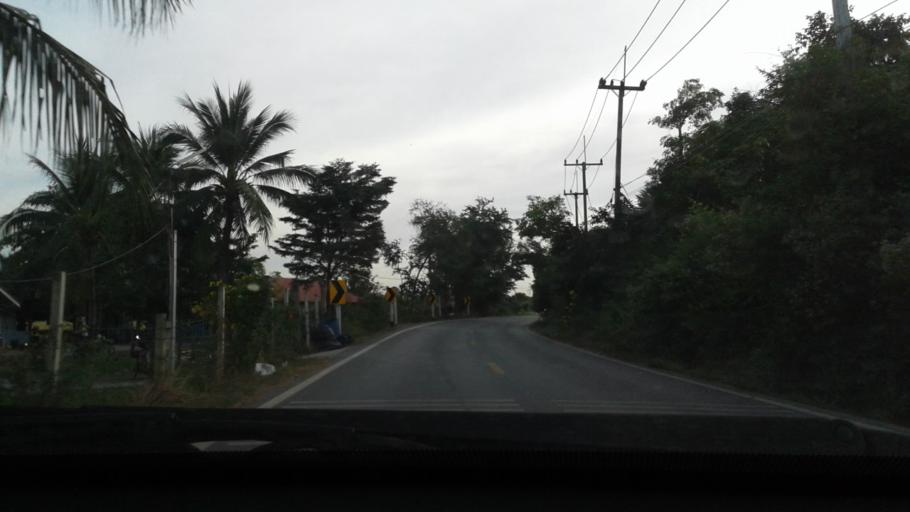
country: TH
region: Nonthaburi
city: Sai Noi
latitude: 13.9200
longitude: 100.2545
